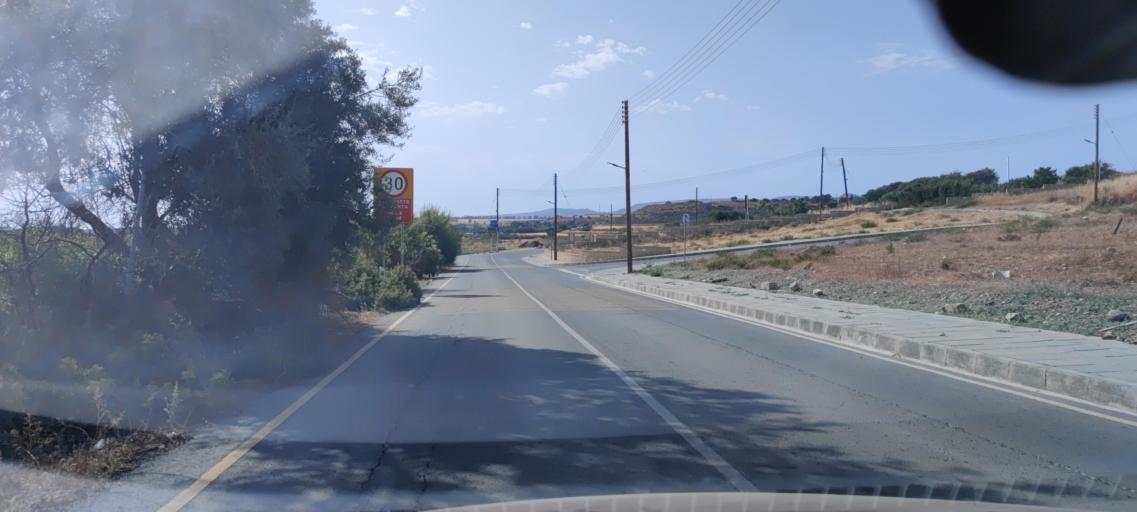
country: CY
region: Limassol
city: Pissouri
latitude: 34.7067
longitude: 32.5687
